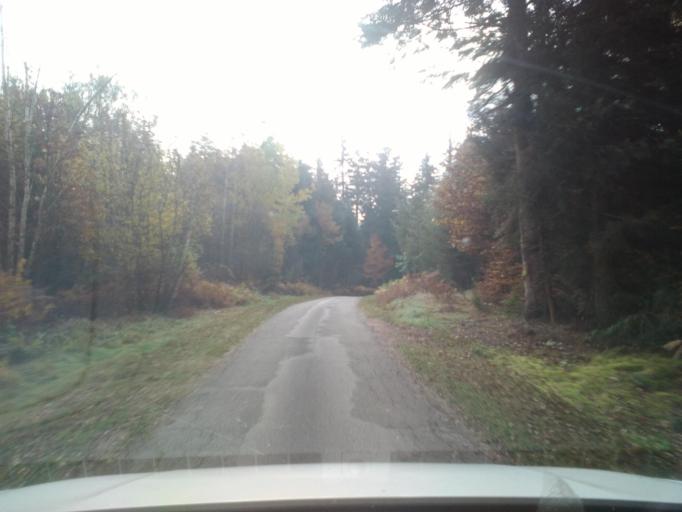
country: FR
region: Lorraine
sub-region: Departement des Vosges
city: Moyenmoutier
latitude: 48.3559
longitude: 6.9027
